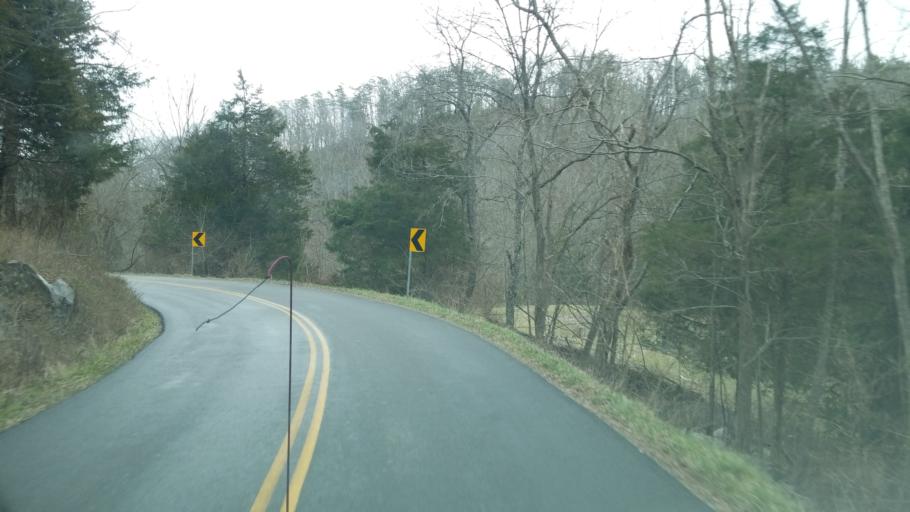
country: US
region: Virginia
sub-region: Giles County
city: Pembroke
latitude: 37.2482
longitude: -80.6913
